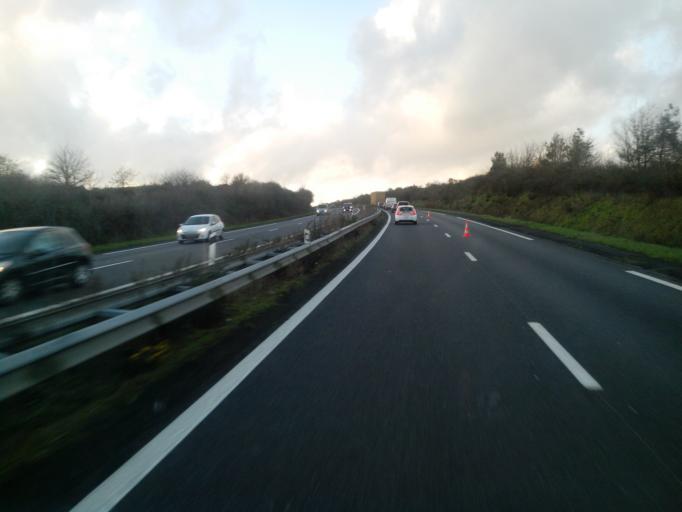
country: FR
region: Pays de la Loire
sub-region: Departement de la Loire-Atlantique
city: La Regrippiere
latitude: 47.1528
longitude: -1.1995
